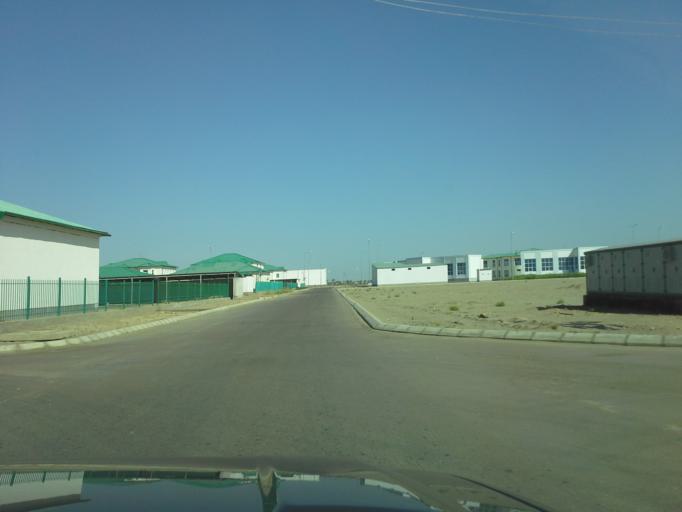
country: TM
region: Dasoguz
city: Dasoguz
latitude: 41.8044
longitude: 59.9477
